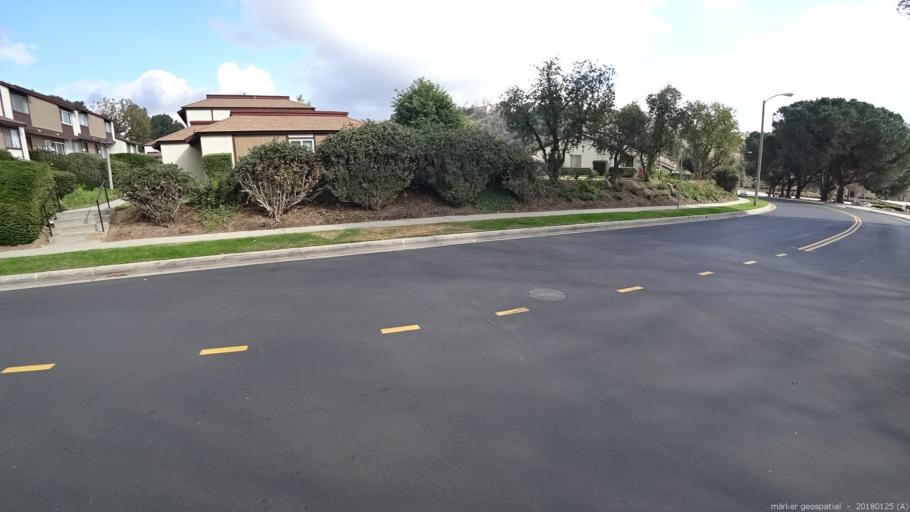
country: US
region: California
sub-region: Los Angeles County
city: Diamond Bar
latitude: 33.9840
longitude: -117.8310
